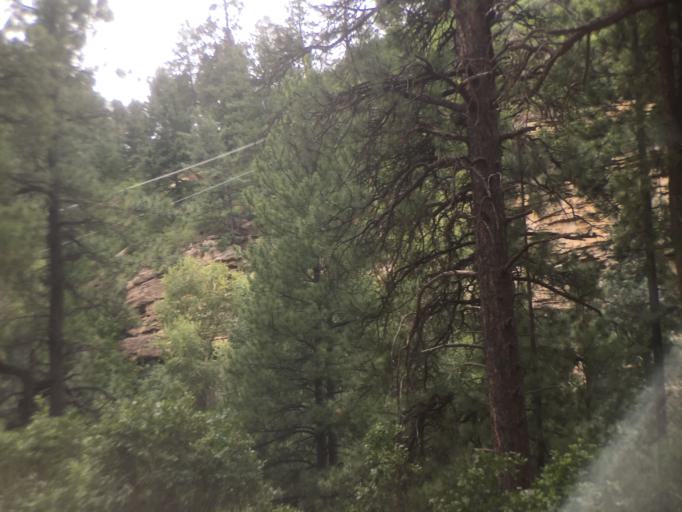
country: US
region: Colorado
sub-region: La Plata County
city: Durango
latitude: 37.3371
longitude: -107.9192
